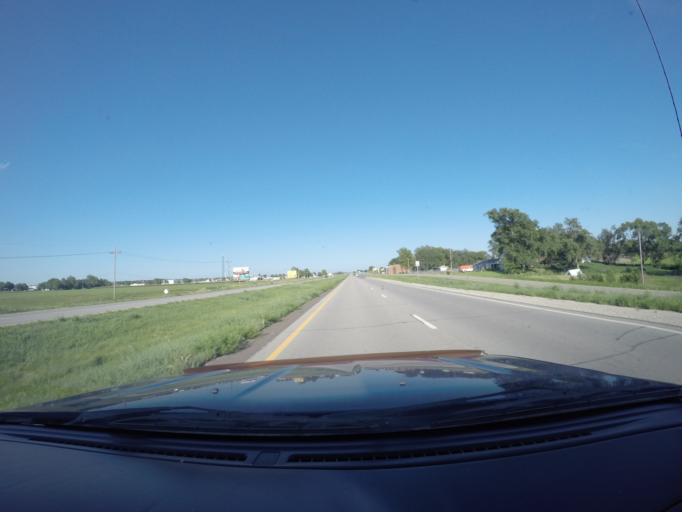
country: US
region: Kansas
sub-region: Shawnee County
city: Topeka
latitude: 39.0907
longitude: -95.7105
